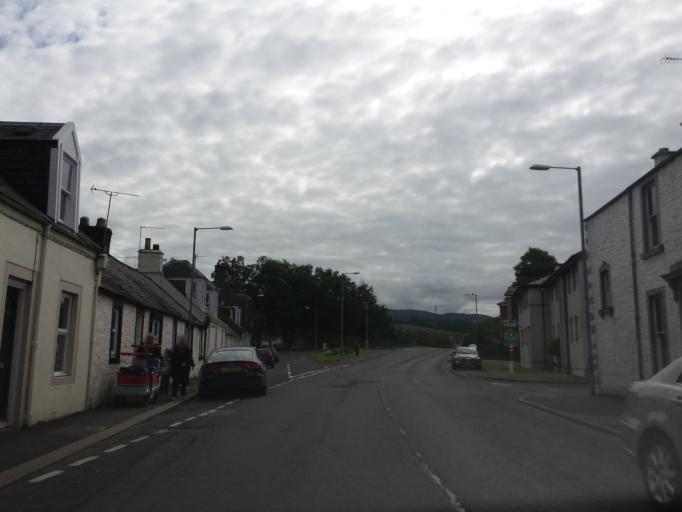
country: GB
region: Scotland
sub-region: Dumfries and Galloway
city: Moffat
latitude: 55.3319
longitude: -3.4426
